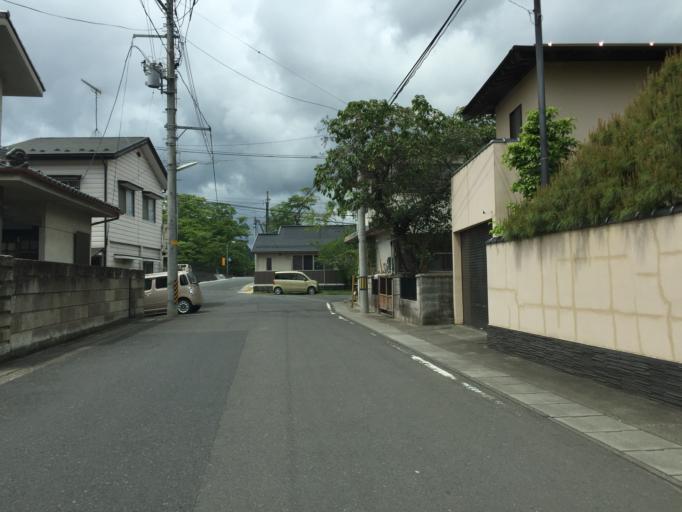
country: JP
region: Fukushima
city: Ishikawa
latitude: 37.0278
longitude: 140.3877
